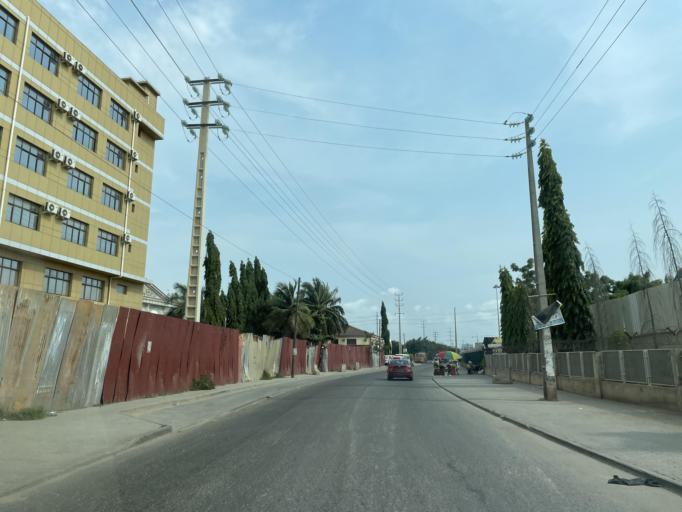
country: AO
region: Luanda
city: Luanda
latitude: -8.9007
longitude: 13.1928
